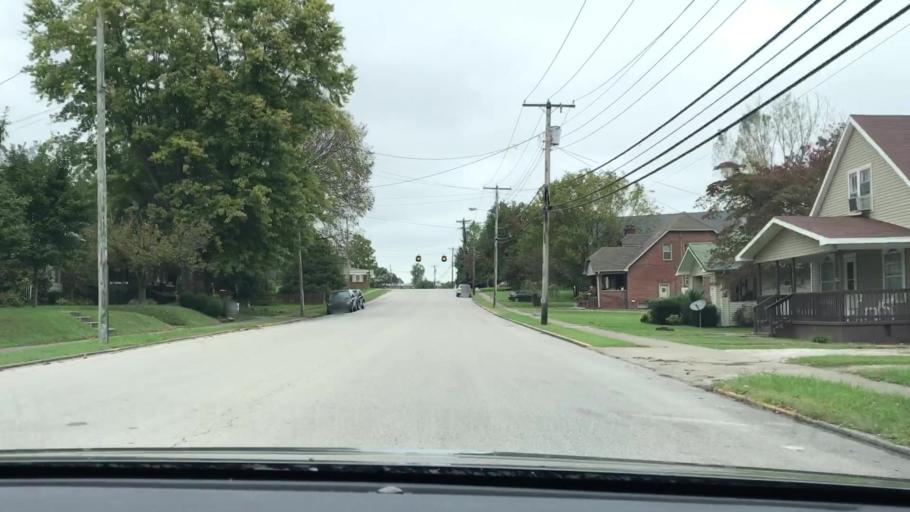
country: US
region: Kentucky
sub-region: Pulaski County
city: Somerset
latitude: 37.0872
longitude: -84.5992
